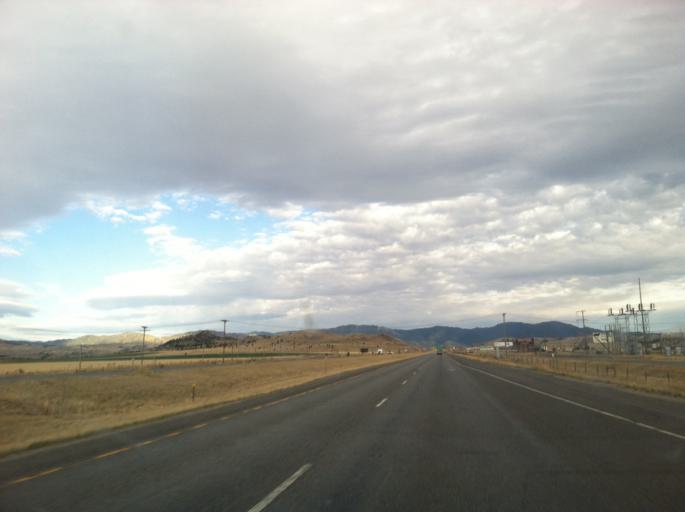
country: US
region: Montana
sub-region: Silver Bow County
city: Butte-Silver Bow (Balance)
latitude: 46.0092
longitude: -112.6789
